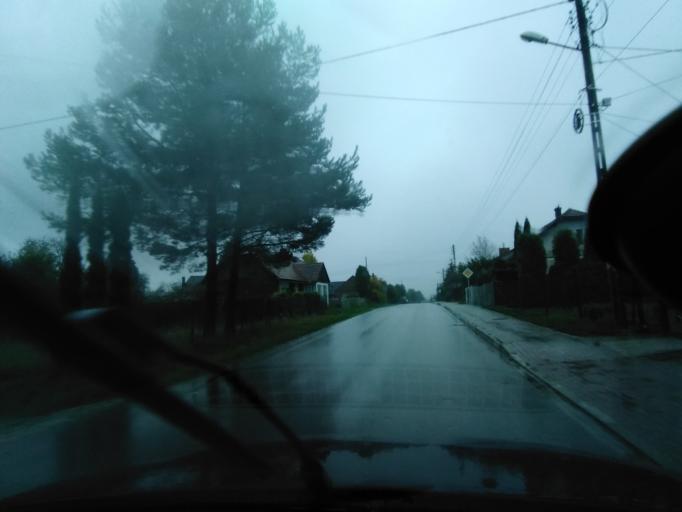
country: PL
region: Subcarpathian Voivodeship
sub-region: Powiat krosnienski
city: Miejsce Piastowe
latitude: 49.6525
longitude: 21.8078
